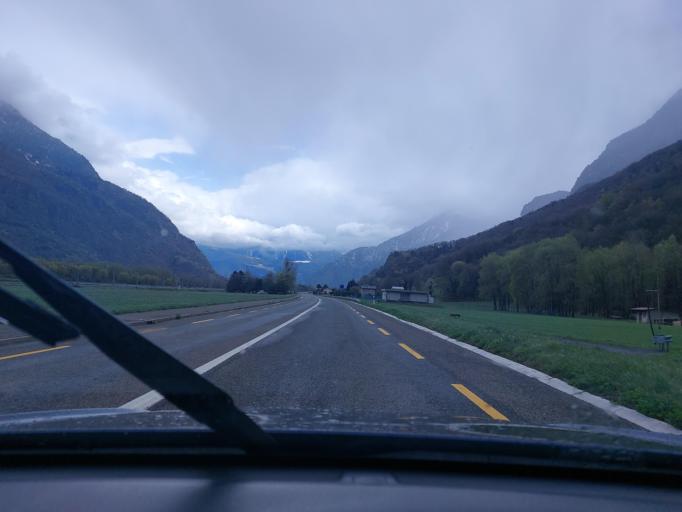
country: CH
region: Valais
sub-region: Martigny District
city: Evionnaz
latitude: 46.1641
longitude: 7.0265
